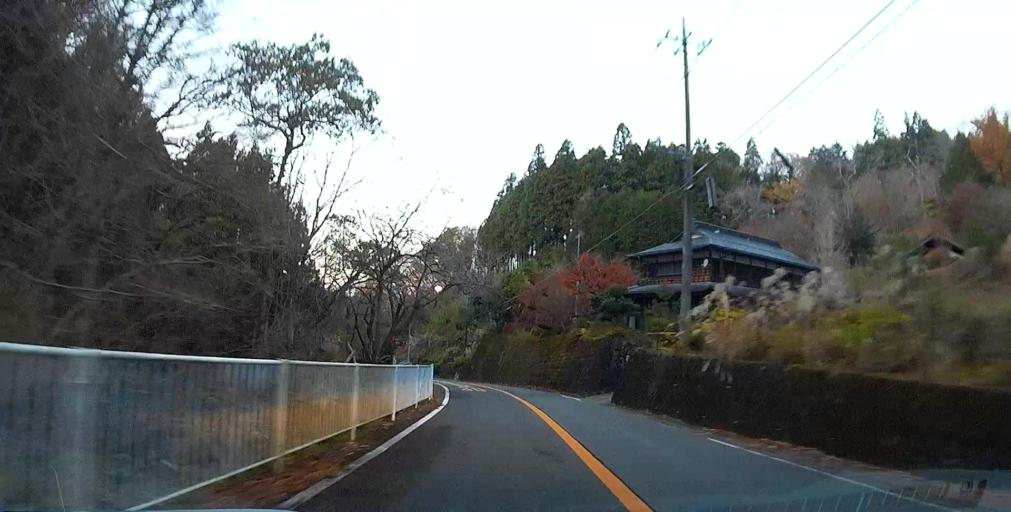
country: JP
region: Yamanashi
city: Uenohara
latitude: 35.5834
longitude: 139.1761
